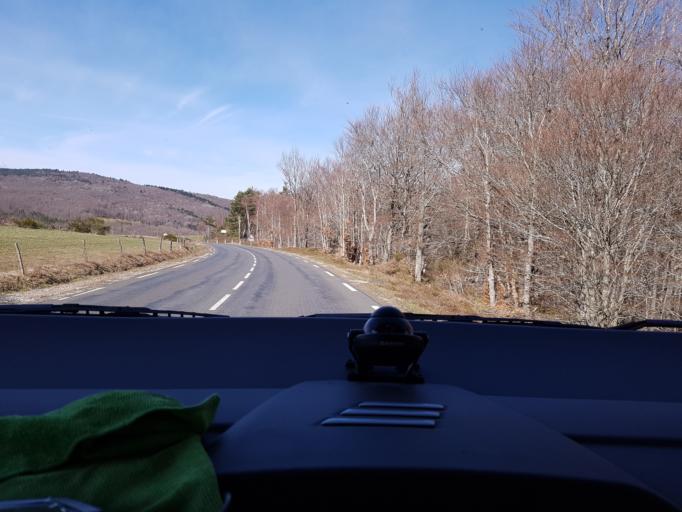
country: FR
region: Auvergne
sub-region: Departement du Cantal
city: Chaudes-Aigues
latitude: 44.8186
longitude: 2.9539
